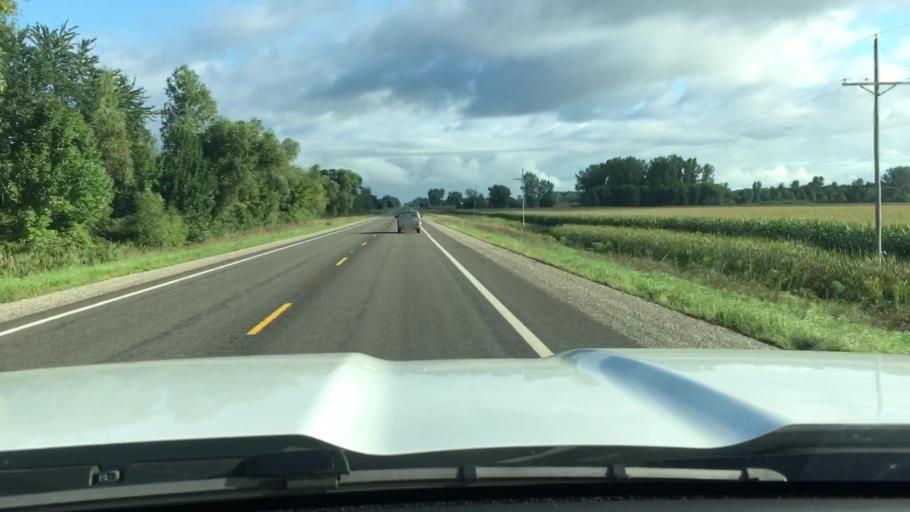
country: US
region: Michigan
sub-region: Tuscola County
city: Caro
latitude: 43.3756
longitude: -83.3832
